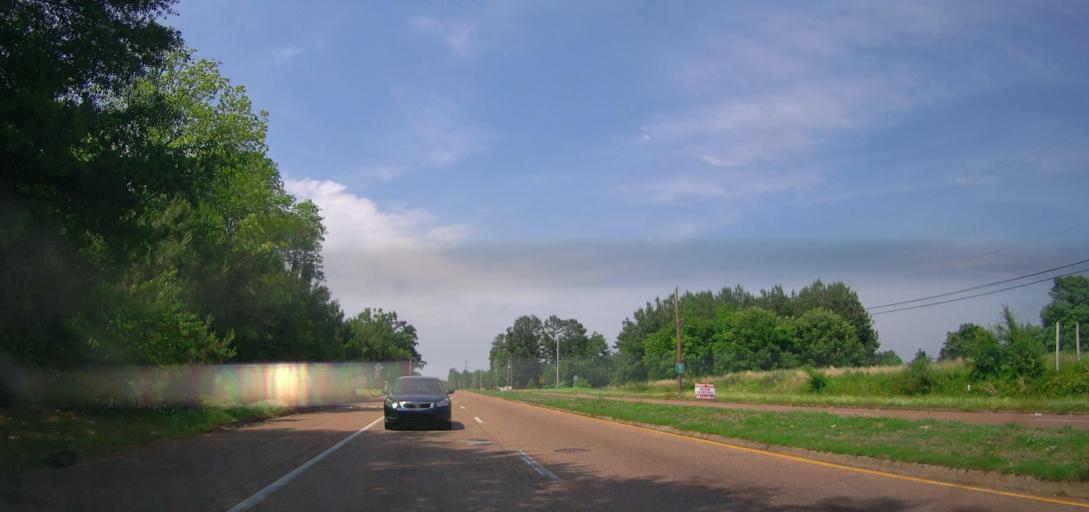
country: US
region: Mississippi
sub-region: De Soto County
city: Olive Branch
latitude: 34.9954
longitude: -89.8309
